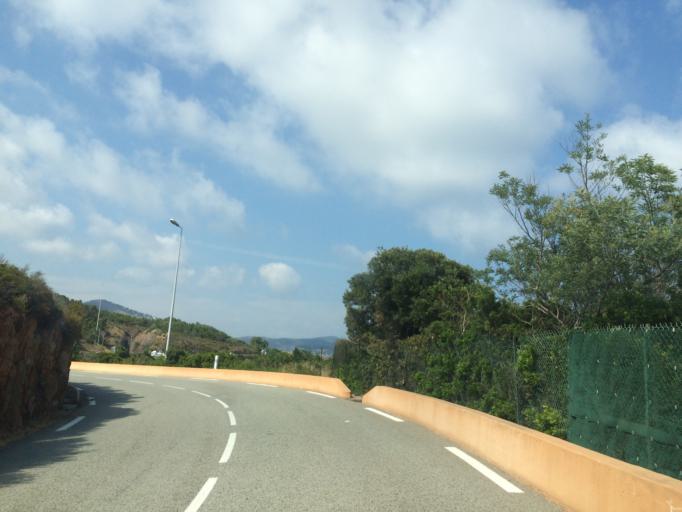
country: FR
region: Provence-Alpes-Cote d'Azur
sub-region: Departement des Alpes-Maritimes
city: Theoule-sur-Mer
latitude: 43.4517
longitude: 6.9200
